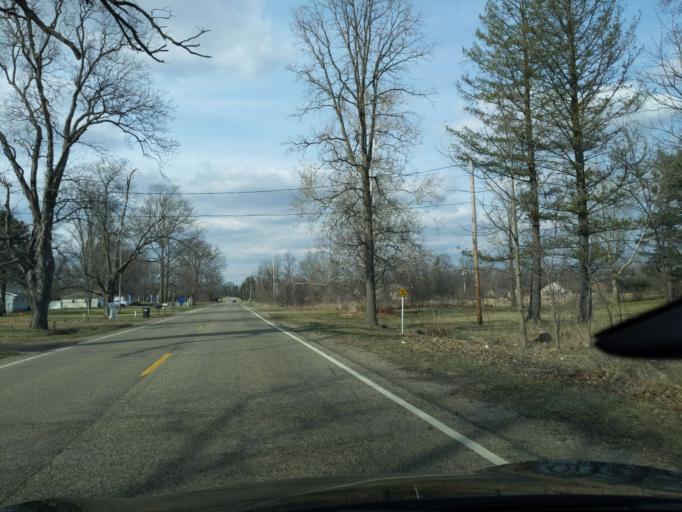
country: US
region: Michigan
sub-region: Jackson County
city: Jackson
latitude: 42.3353
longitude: -84.4136
